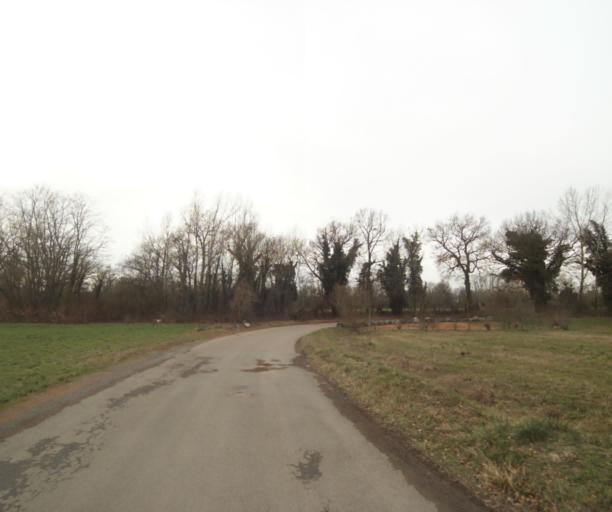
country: FR
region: Rhone-Alpes
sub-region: Departement de la Loire
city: Perreux
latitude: 46.0609
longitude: 4.1061
